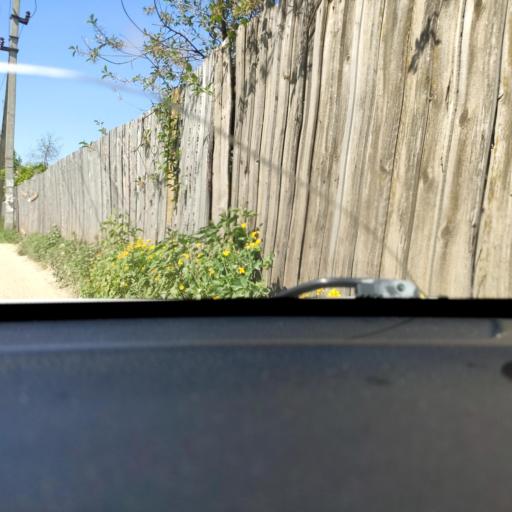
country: RU
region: Tatarstan
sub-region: Gorod Kazan'
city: Kazan
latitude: 55.8628
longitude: 49.1976
